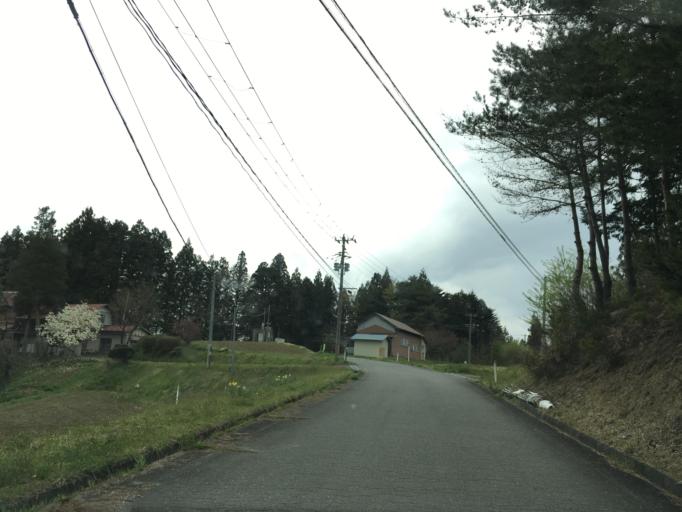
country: JP
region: Iwate
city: Ichinoseki
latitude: 38.8560
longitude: 141.3246
